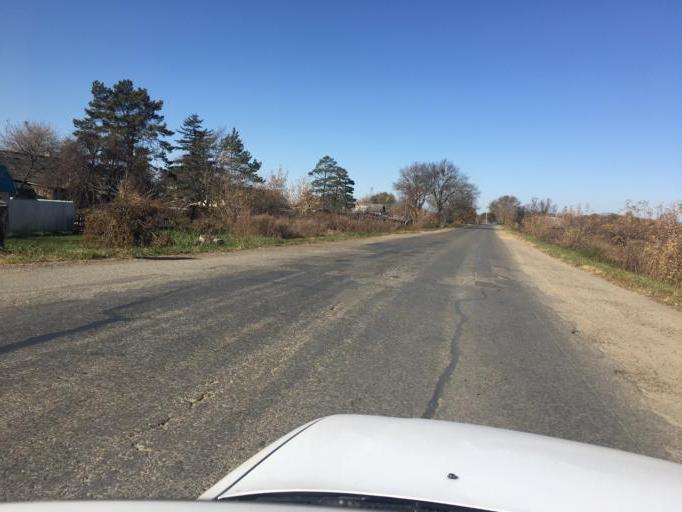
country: RU
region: Primorskiy
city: Dal'nerechensk
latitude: 45.9126
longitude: 133.7930
